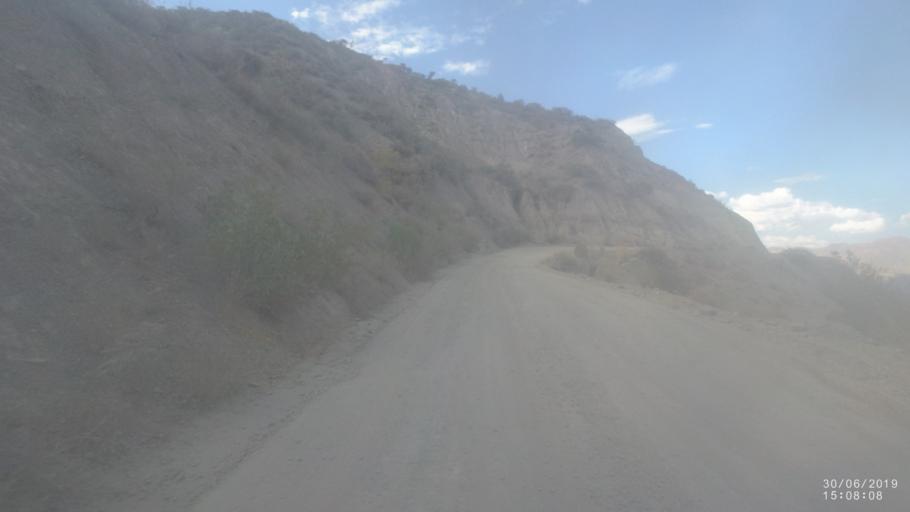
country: BO
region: Cochabamba
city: Irpa Irpa
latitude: -17.7313
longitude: -66.3037
